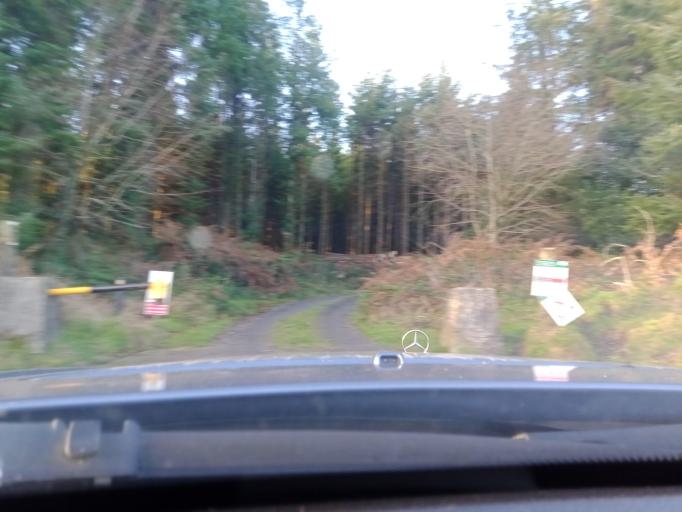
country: IE
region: Leinster
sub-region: Kilkenny
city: Graiguenamanagh
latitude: 52.4882
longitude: -6.9561
